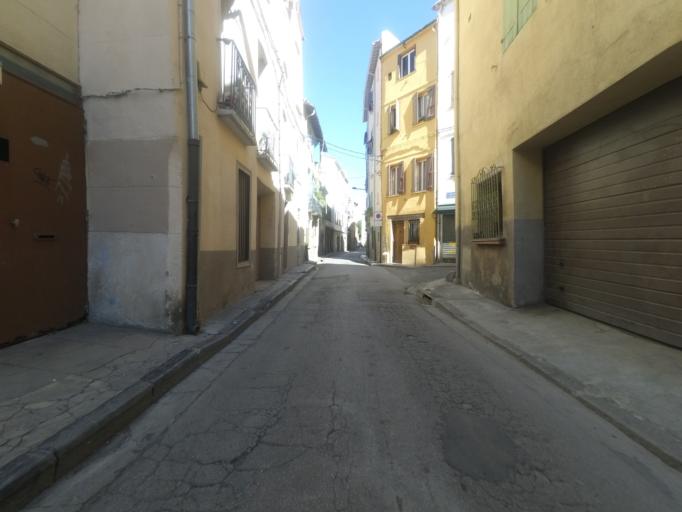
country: FR
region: Languedoc-Roussillon
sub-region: Departement des Pyrenees-Orientales
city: Perpignan
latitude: 42.6989
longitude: 2.8986
